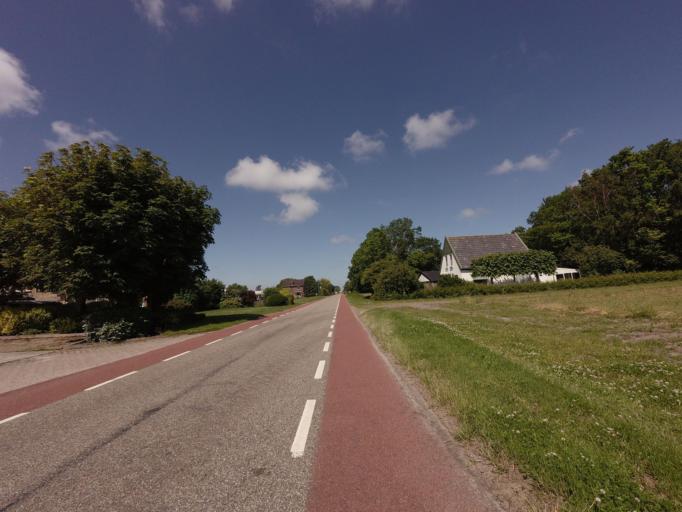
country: NL
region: North Holland
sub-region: Gemeente Den Helder
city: Den Helder
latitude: 52.8984
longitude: 4.8185
